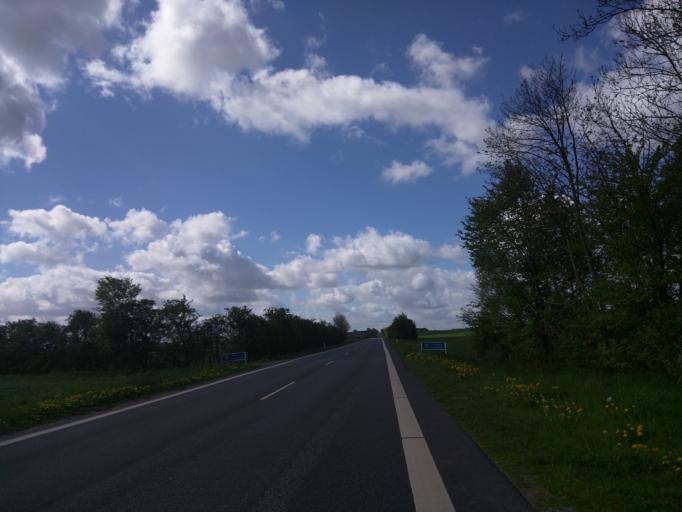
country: DK
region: Central Jutland
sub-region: Silkeborg Kommune
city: Kjellerup
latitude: 56.3695
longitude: 9.4395
